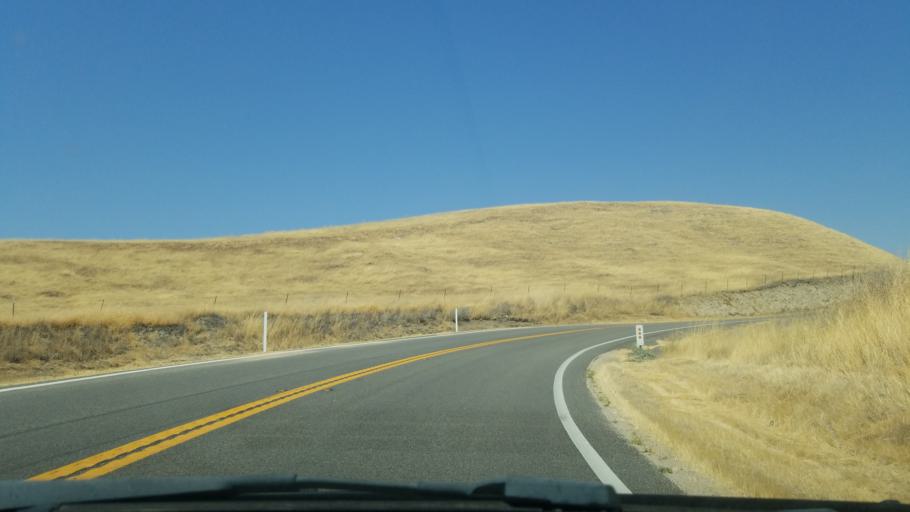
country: US
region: California
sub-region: San Luis Obispo County
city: Shandon
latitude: 35.5875
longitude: -120.4272
